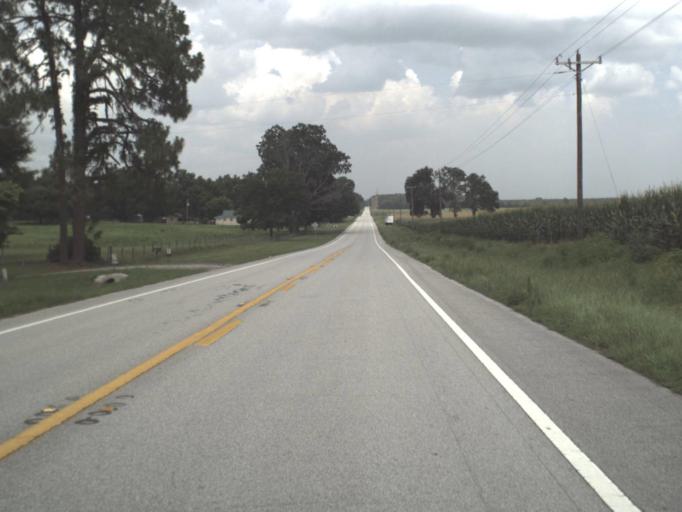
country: US
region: Florida
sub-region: Madison County
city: Madison
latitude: 30.4722
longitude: -83.2963
